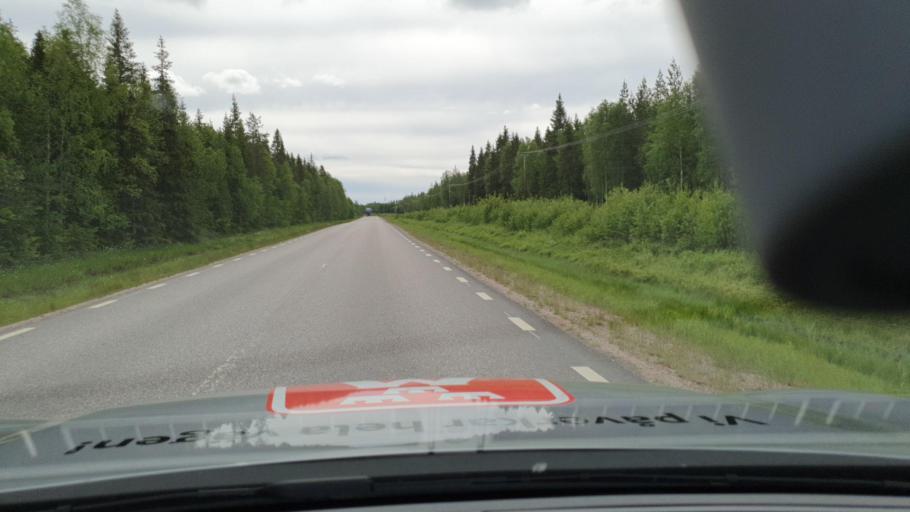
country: SE
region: Norrbotten
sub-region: Kalix Kommun
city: Kalix
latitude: 65.9045
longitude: 23.4580
